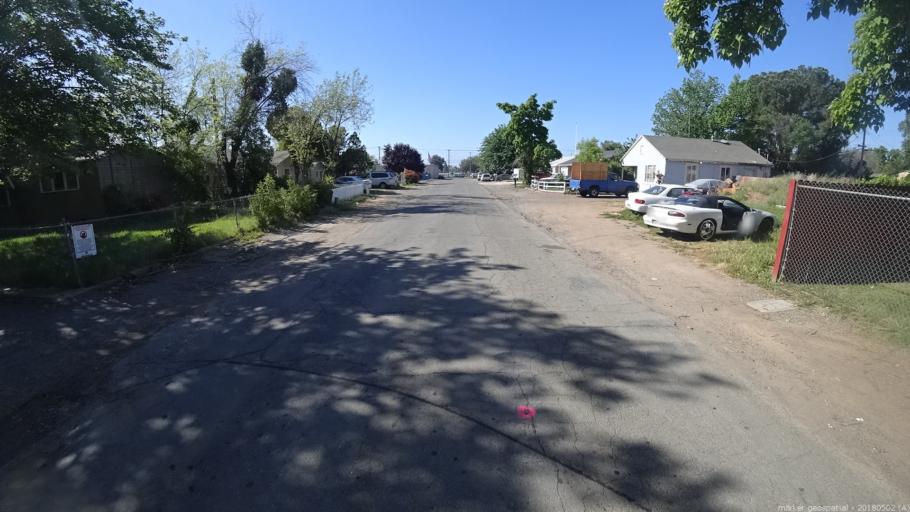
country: US
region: California
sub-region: Sacramento County
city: Arden-Arcade
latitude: 38.6101
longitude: -121.4305
